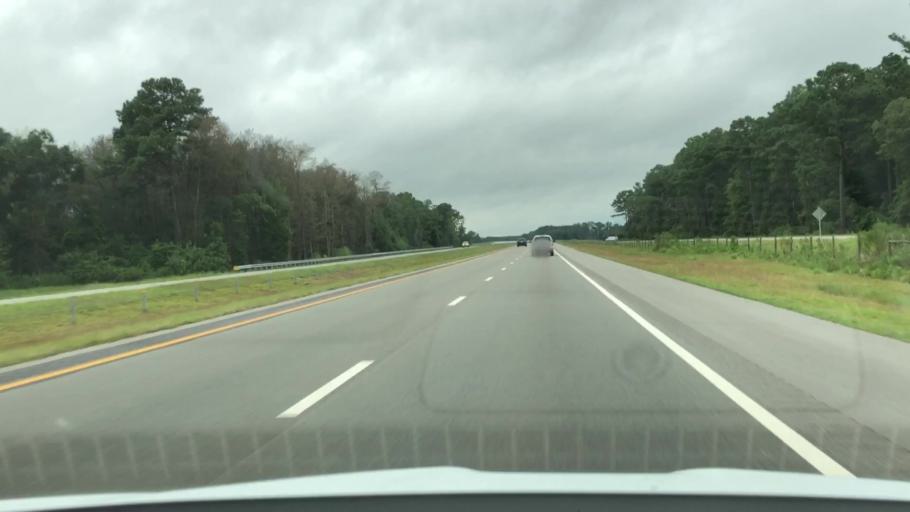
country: US
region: North Carolina
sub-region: Wayne County
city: Elroy
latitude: 35.3490
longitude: -77.8470
